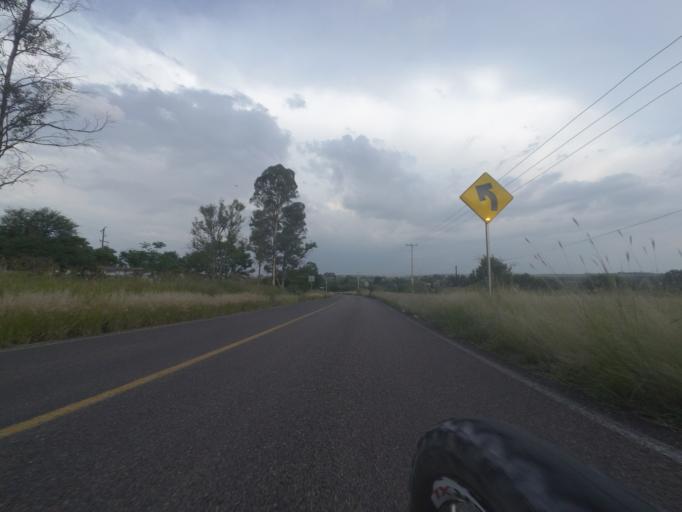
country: MX
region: Aguascalientes
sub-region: Aguascalientes
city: La Loma de los Negritos
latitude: 21.8366
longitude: -102.3730
